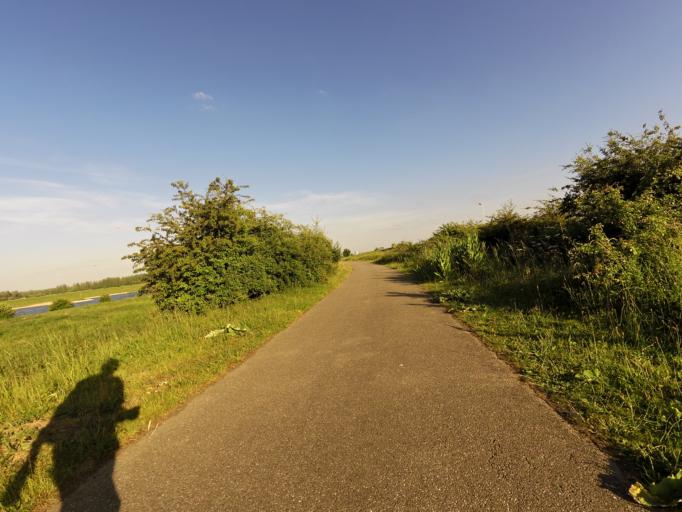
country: NL
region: Gelderland
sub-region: Gemeente Duiven
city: Duiven
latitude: 51.8826
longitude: 6.0258
